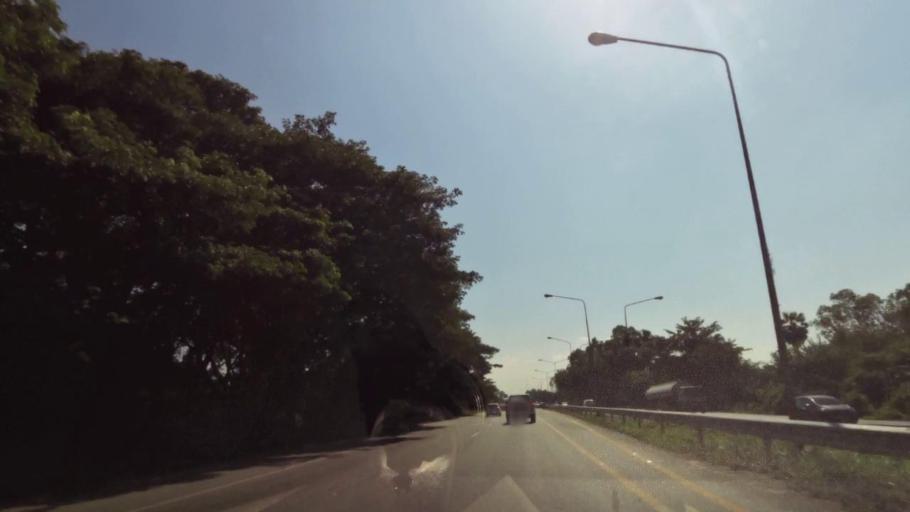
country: TH
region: Nakhon Sawan
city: Kao Liao
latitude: 15.7831
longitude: 100.1211
